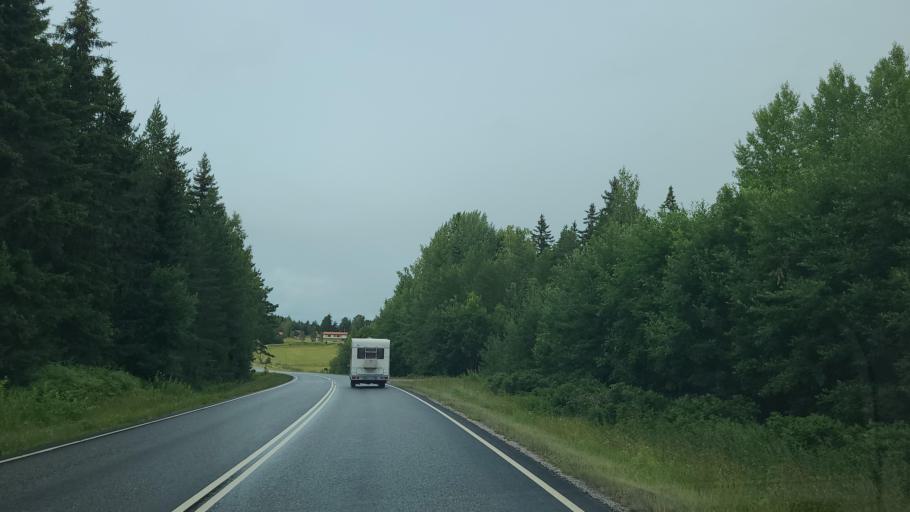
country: FI
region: Varsinais-Suomi
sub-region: Turku
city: Sauvo
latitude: 60.2859
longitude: 22.6739
